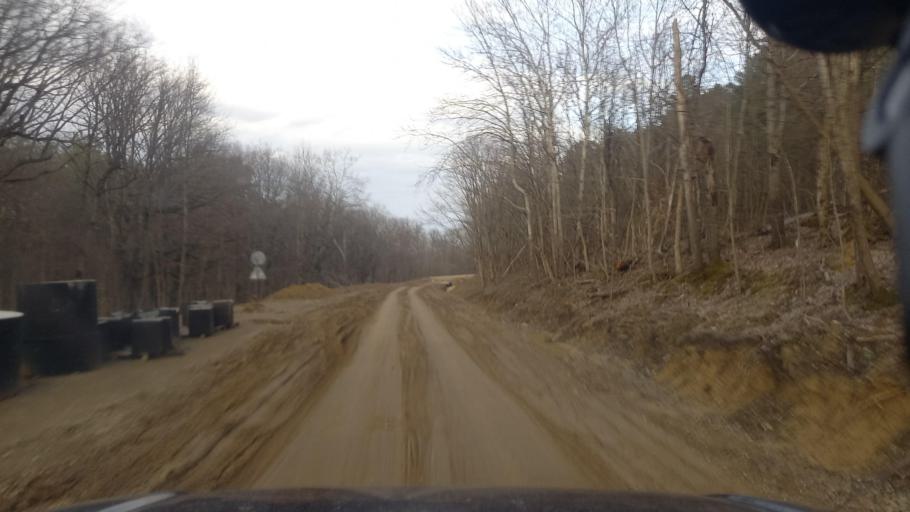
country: RU
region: Krasnodarskiy
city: Goryachiy Klyuch
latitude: 44.6988
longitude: 38.9922
